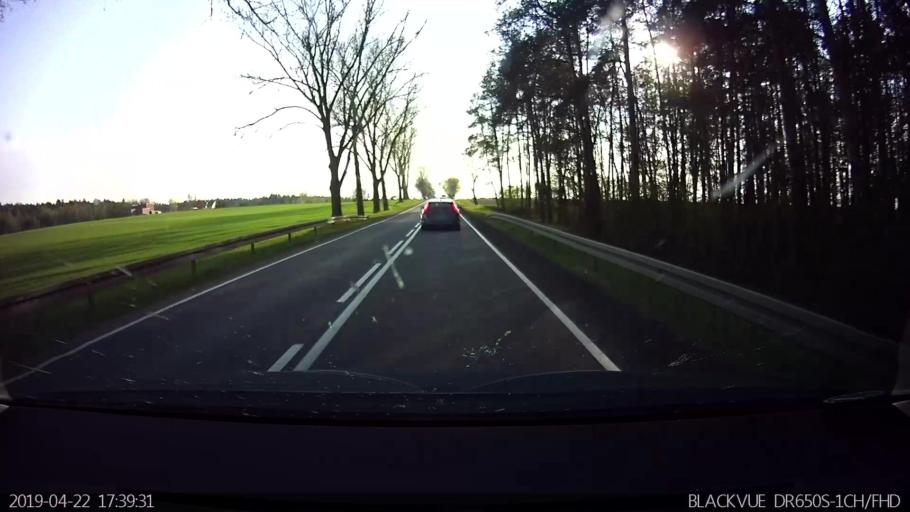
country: PL
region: Masovian Voivodeship
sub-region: Powiat wegrowski
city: Miedzna
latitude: 52.4016
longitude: 22.1405
